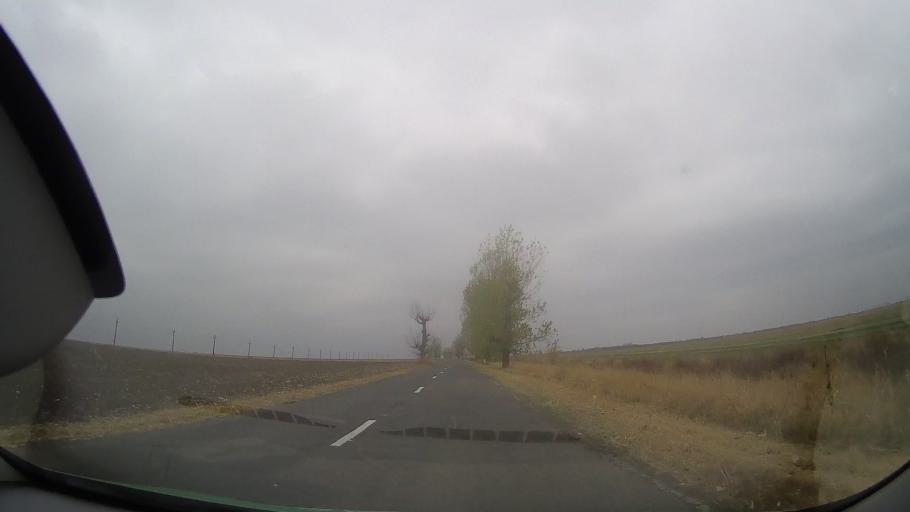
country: RO
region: Ialomita
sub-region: Comuna Grindu
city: Grindu
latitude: 44.7965
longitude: 26.8880
